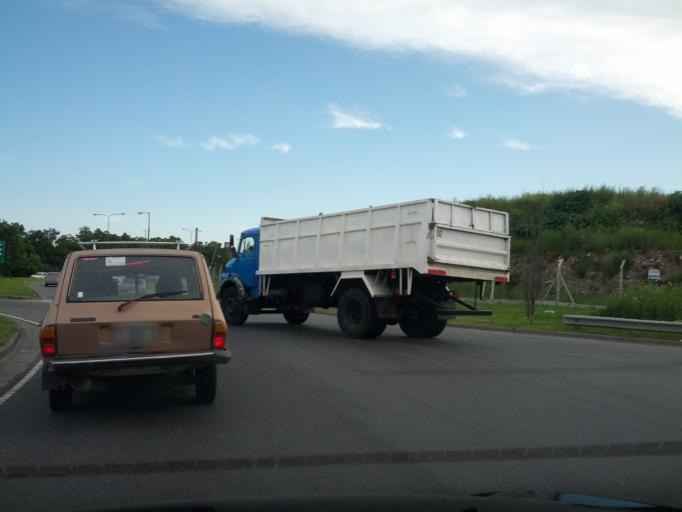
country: AR
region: Buenos Aires F.D.
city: Villa Lugano
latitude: -34.6737
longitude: -58.4360
